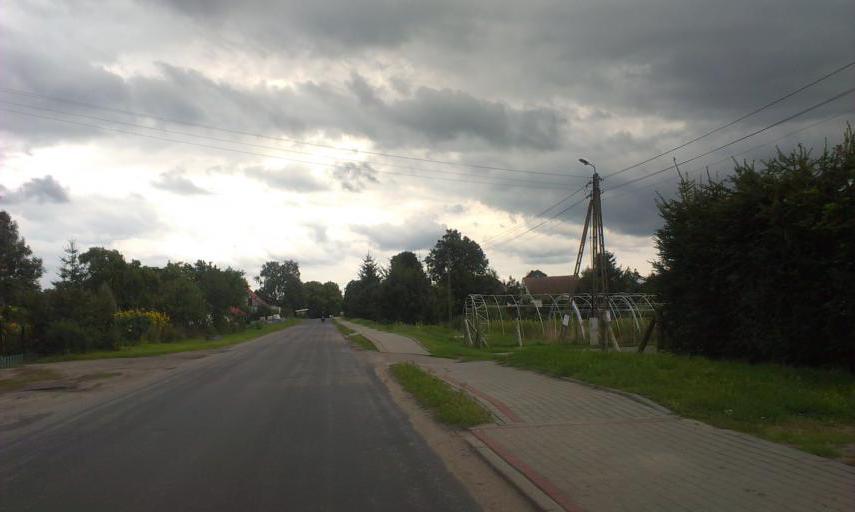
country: PL
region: West Pomeranian Voivodeship
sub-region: Powiat bialogardzki
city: Tychowo
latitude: 53.9376
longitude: 16.2378
